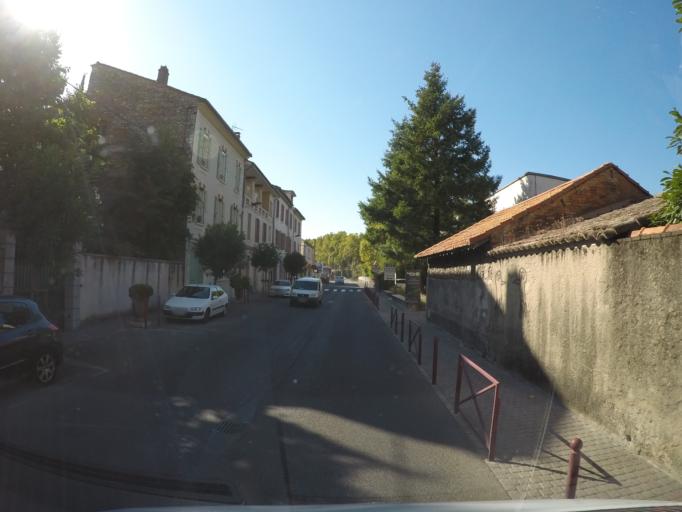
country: FR
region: Languedoc-Roussillon
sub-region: Departement du Gard
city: Anduze
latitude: 44.0515
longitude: 3.9852
